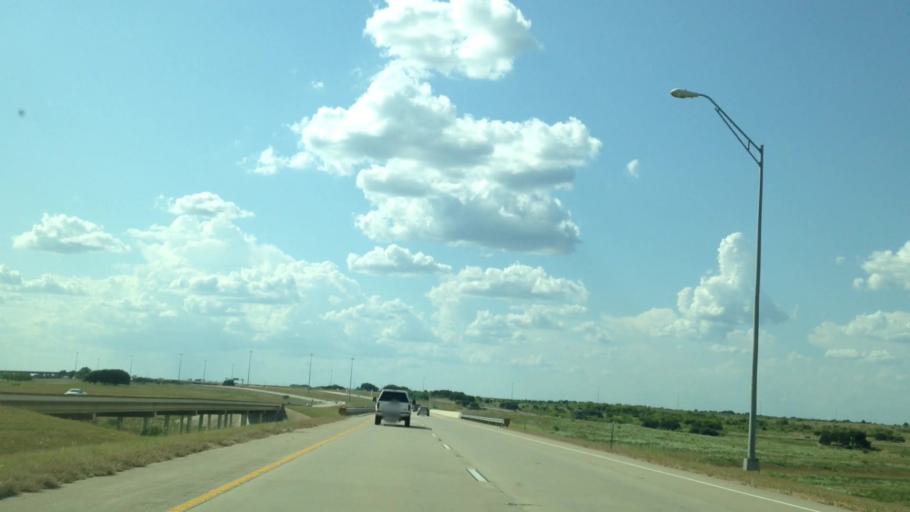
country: US
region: Texas
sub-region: Travis County
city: Onion Creek
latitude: 30.1059
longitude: -97.7877
